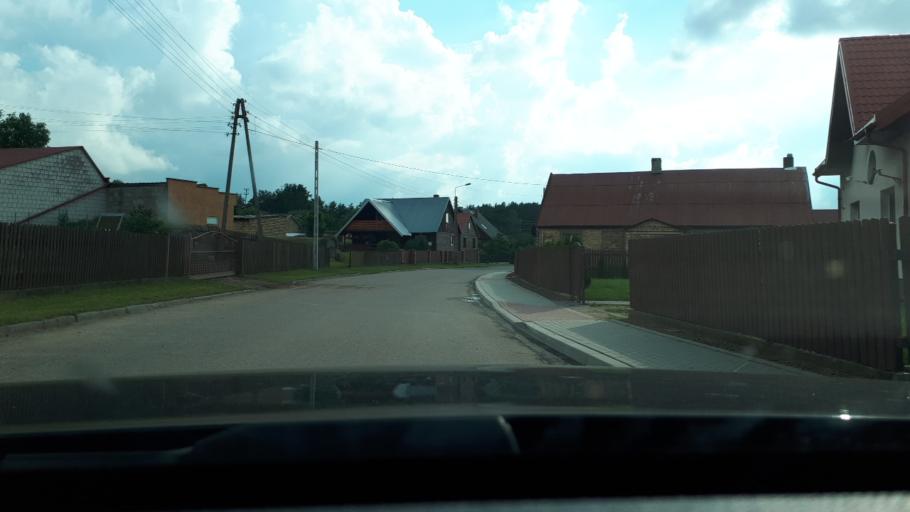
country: PL
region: Podlasie
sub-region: Powiat moniecki
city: Knyszyn
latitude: 53.2734
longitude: 22.9829
